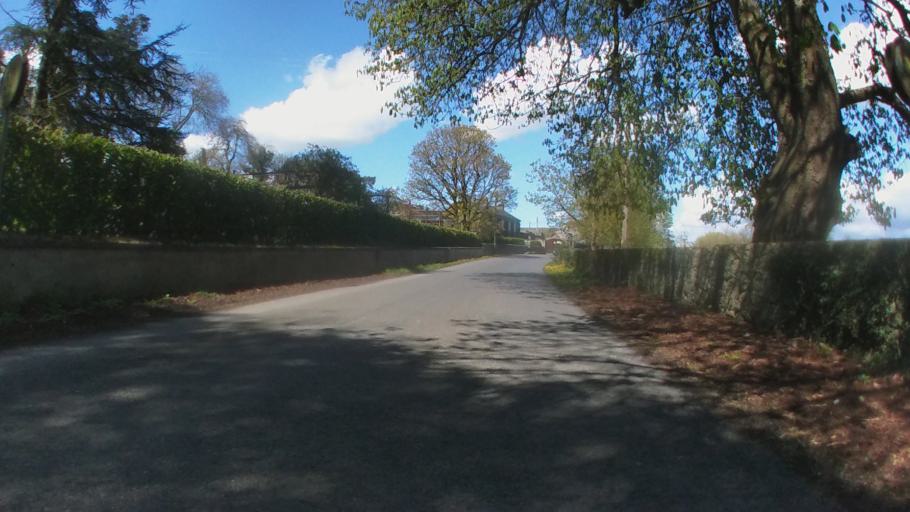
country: IE
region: Leinster
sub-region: Kilkenny
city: Thomastown
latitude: 52.5909
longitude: -7.1876
